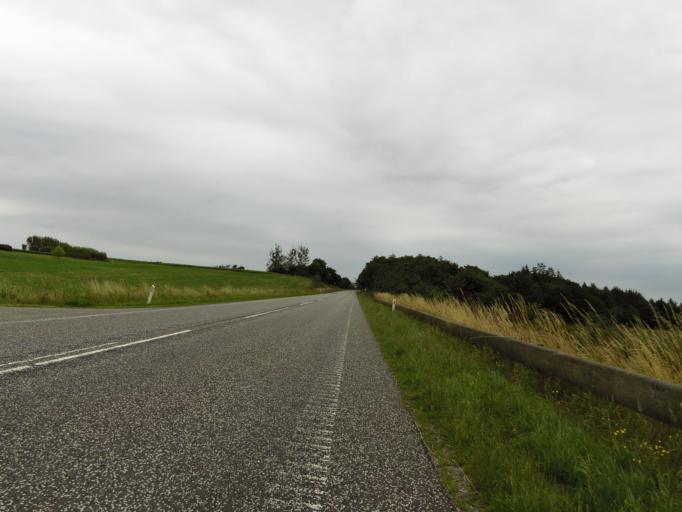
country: DK
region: South Denmark
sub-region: Tonder Kommune
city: Logumkloster
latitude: 55.1177
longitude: 8.9584
